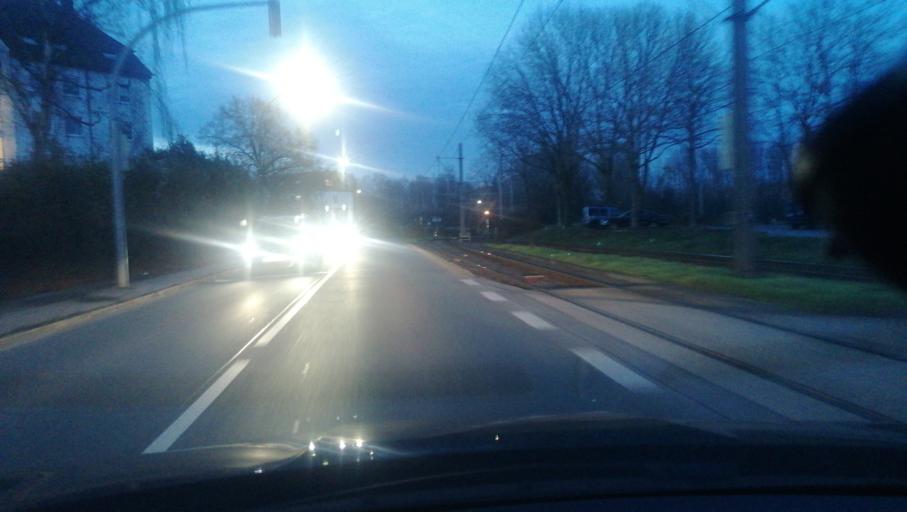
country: DE
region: North Rhine-Westphalia
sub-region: Regierungsbezirk Arnsberg
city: Dortmund
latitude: 51.5322
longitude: 7.4180
